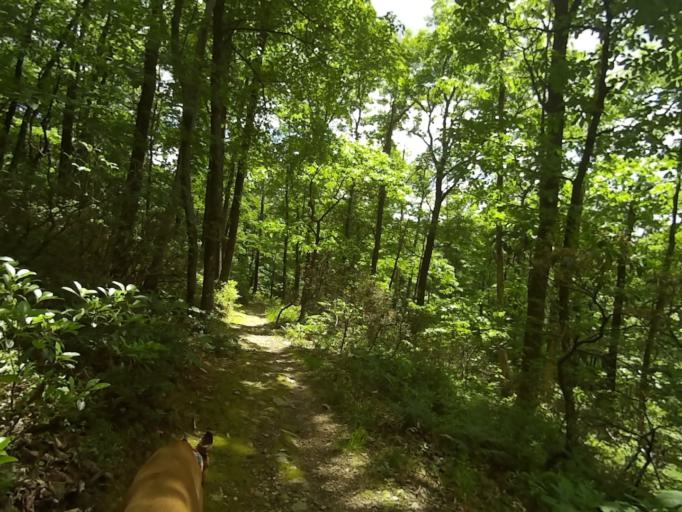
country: US
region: Pennsylvania
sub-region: Centre County
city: Stormstown
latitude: 40.9217
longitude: -78.0563
